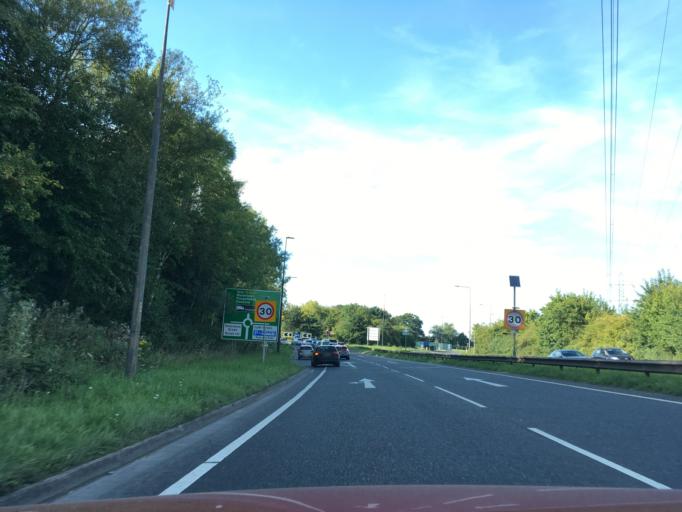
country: GB
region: England
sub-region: South Gloucestershire
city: Siston
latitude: 51.4900
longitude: -2.4696
